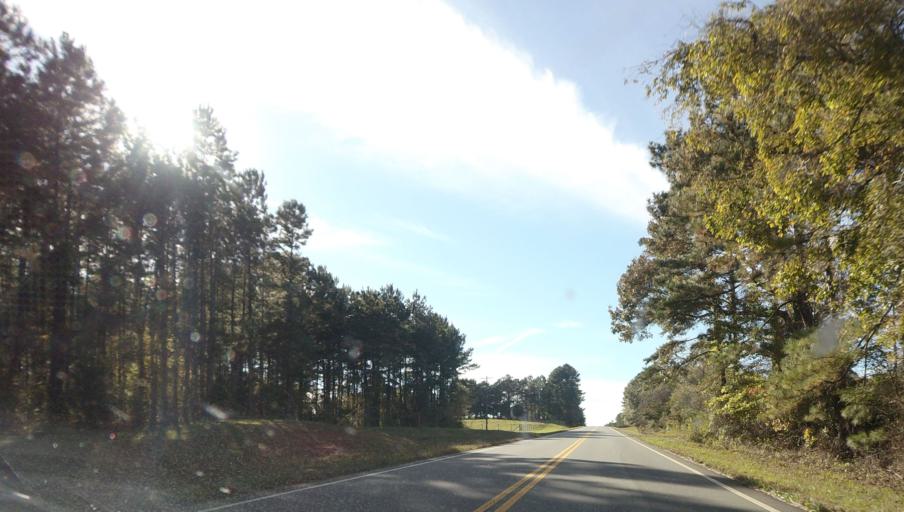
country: US
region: Georgia
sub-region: Talbot County
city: Talbotton
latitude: 32.6888
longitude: -84.4906
